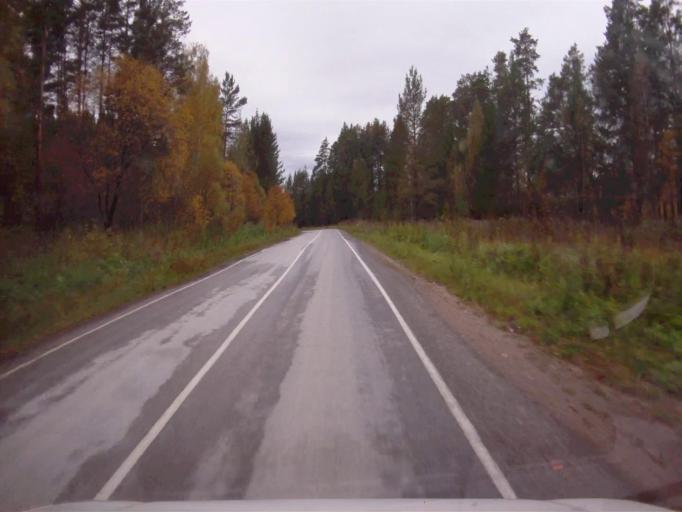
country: RU
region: Chelyabinsk
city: Nyazepetrovsk
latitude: 56.0562
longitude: 59.4719
